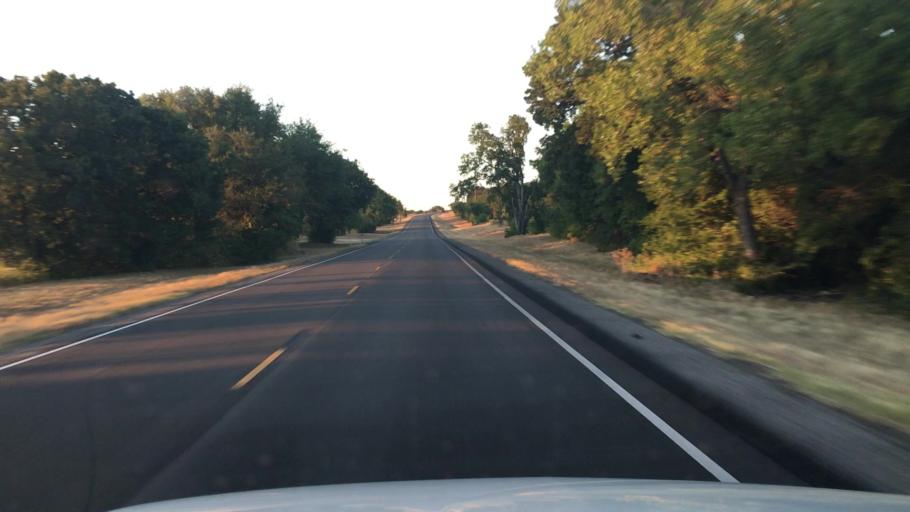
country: US
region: Texas
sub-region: Hamilton County
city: Hico
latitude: 32.0548
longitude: -97.9988
